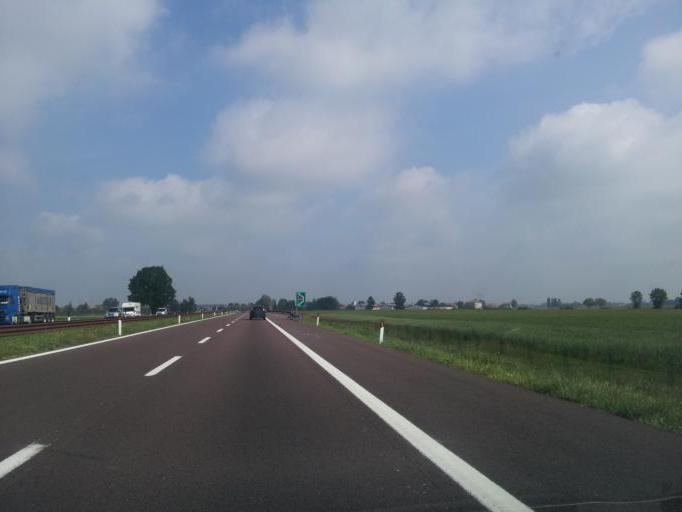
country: IT
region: Lombardy
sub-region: Provincia di Mantova
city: Bondeno
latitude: 44.9480
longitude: 10.8647
